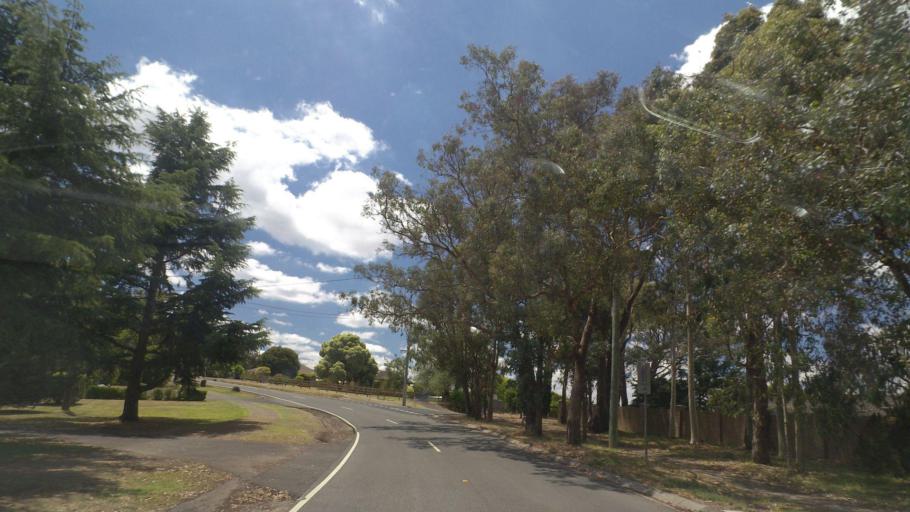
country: AU
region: Victoria
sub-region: Manningham
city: Warrandyte
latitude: -37.7355
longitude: 145.2724
